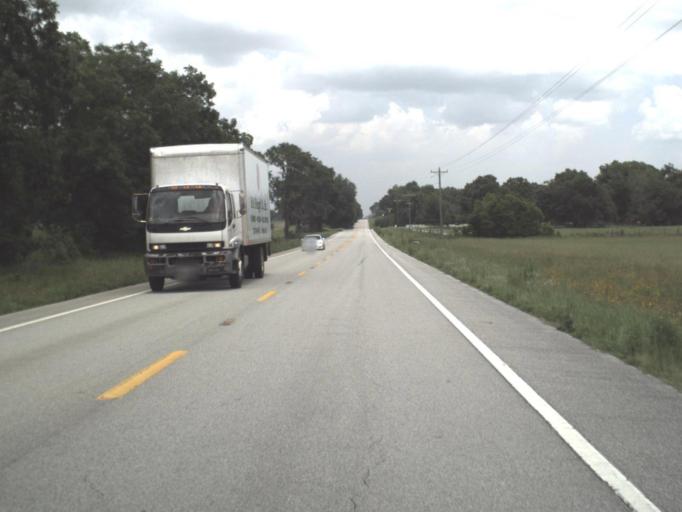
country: US
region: Florida
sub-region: Madison County
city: Madison
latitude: 30.4723
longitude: -83.3184
